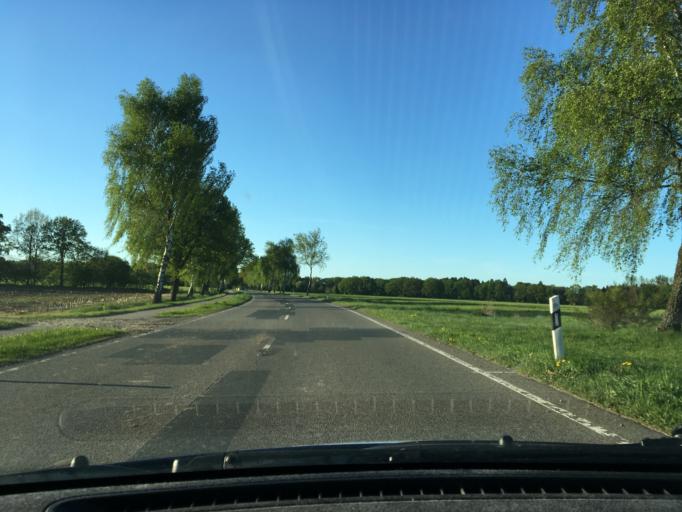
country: DE
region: Lower Saxony
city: Bispingen
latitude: 53.0203
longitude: 9.9995
